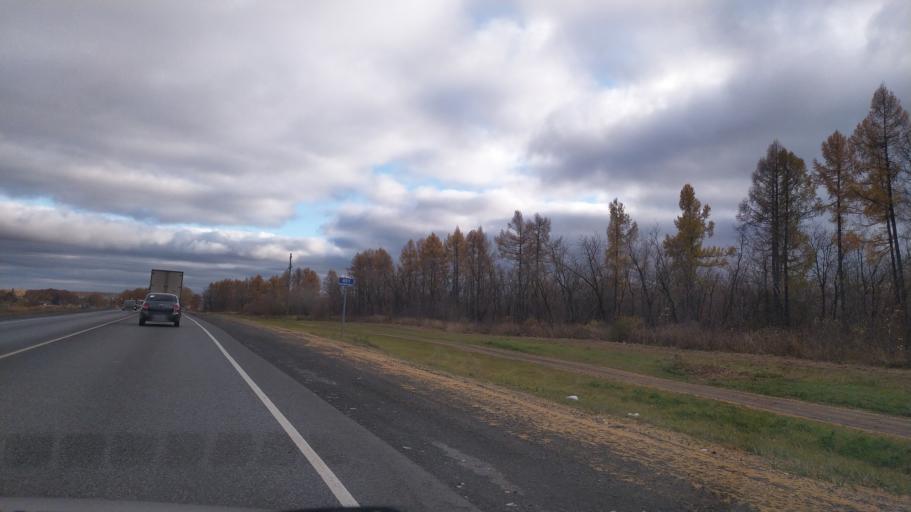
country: RU
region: Chuvashia
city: Novyye Lapsary
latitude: 56.0654
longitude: 47.2394
